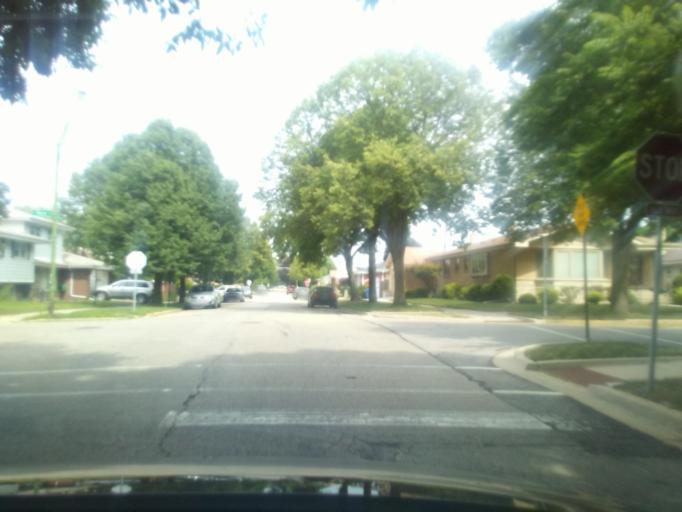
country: US
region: Illinois
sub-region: Cook County
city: Harwood Heights
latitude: 41.9701
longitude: -87.8062
